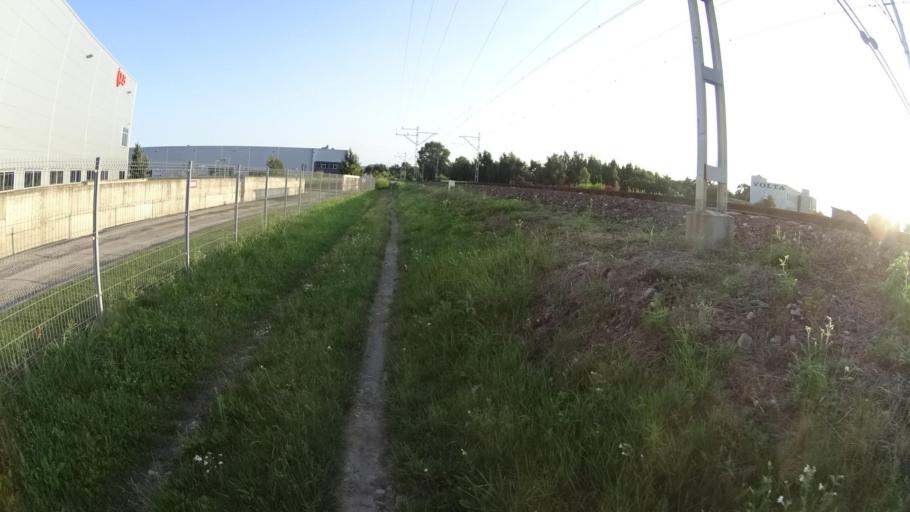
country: PL
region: Masovian Voivodeship
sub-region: Warszawa
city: Wlochy
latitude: 52.1893
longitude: 20.9295
